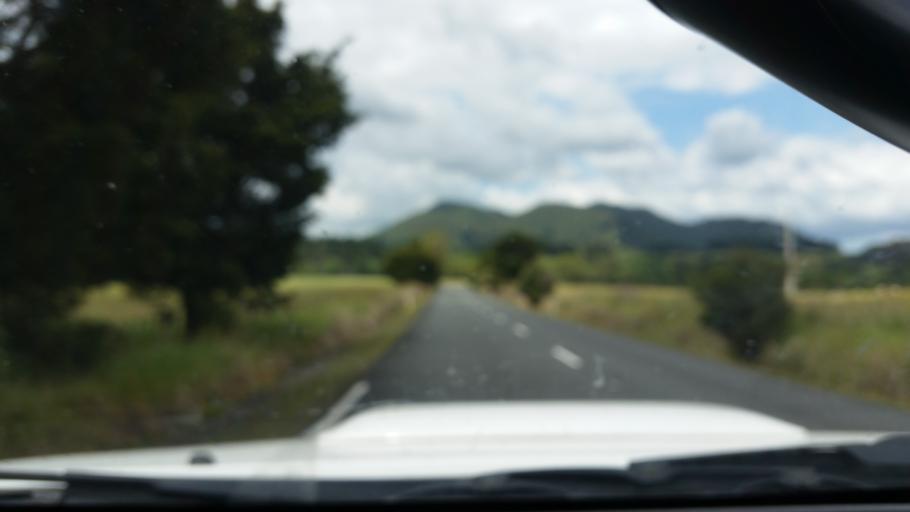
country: NZ
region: Northland
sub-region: Kaipara District
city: Dargaville
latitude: -35.7503
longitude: 173.8941
